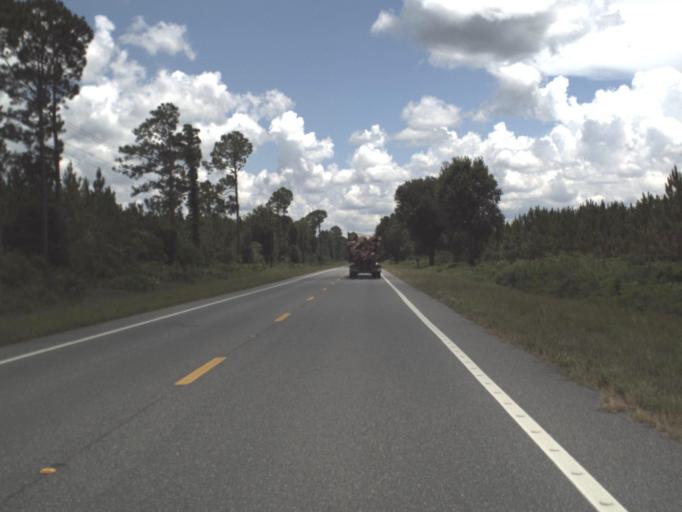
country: US
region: Florida
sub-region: Taylor County
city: Perry
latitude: 30.1428
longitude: -83.8297
